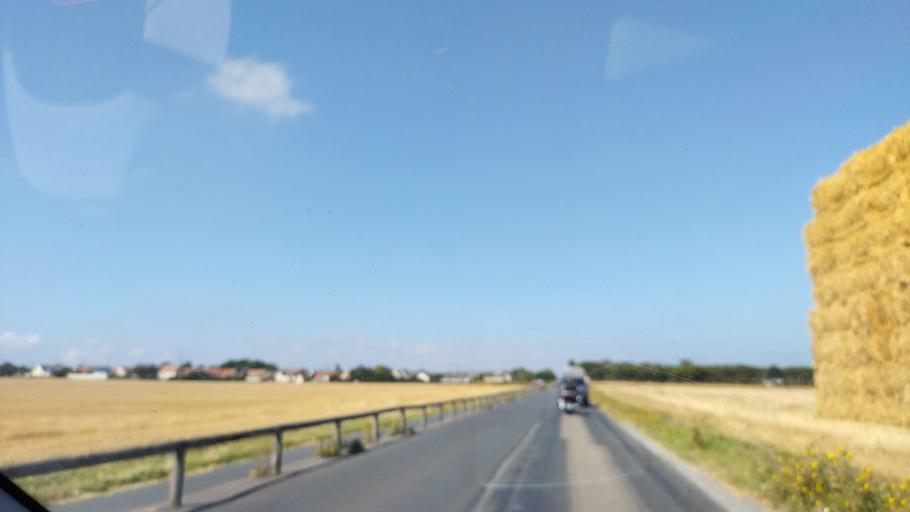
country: FR
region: Lower Normandy
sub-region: Departement du Calvados
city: Bernieres-sur-Mer
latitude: 49.3295
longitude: -0.4361
